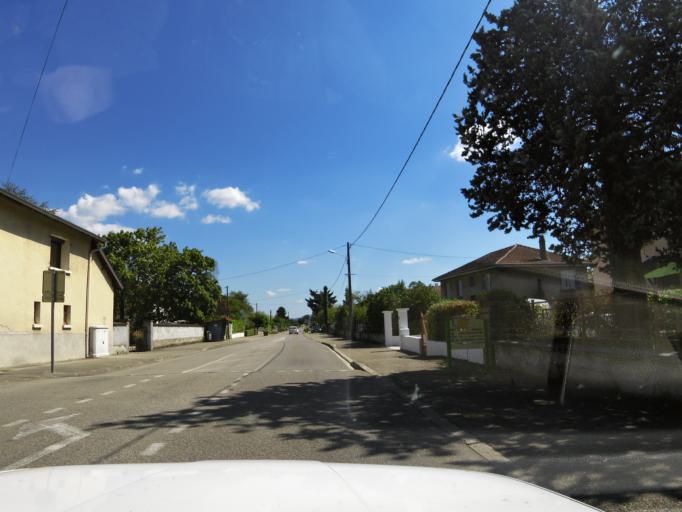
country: FR
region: Rhone-Alpes
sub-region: Departement de l'Ain
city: Saint-Denis-en-Bugey
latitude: 45.9466
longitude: 5.3295
